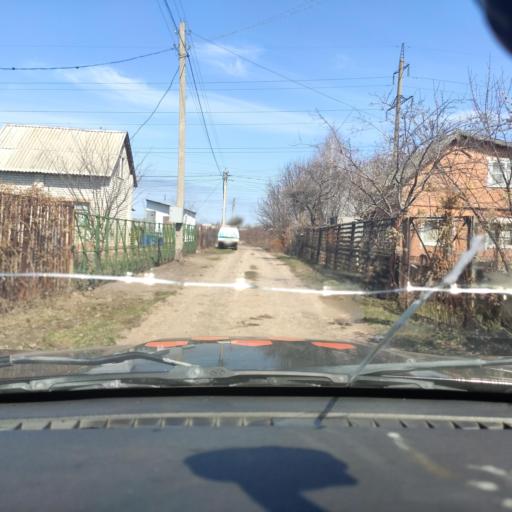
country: RU
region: Samara
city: Tol'yatti
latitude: 53.5866
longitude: 49.3141
